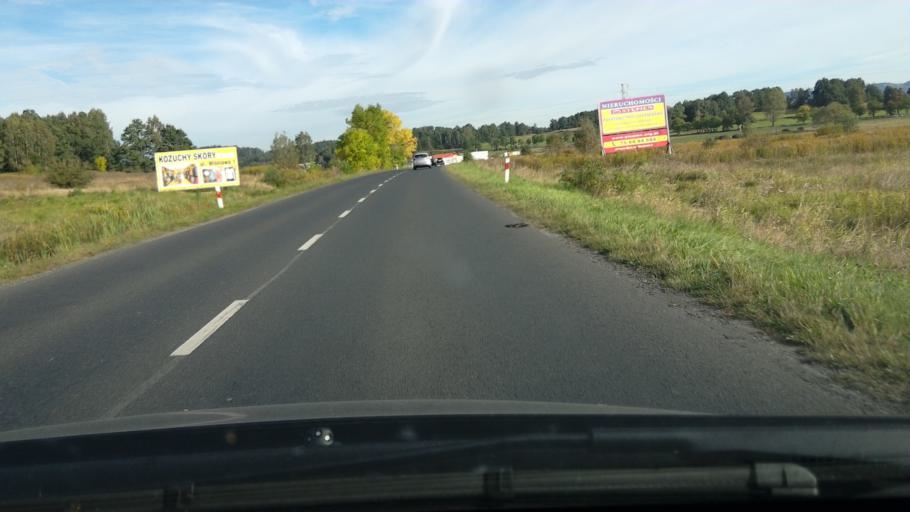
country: PL
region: Lower Silesian Voivodeship
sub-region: Powiat jeleniogorski
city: Myslakowice
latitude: 50.8524
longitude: 15.7738
